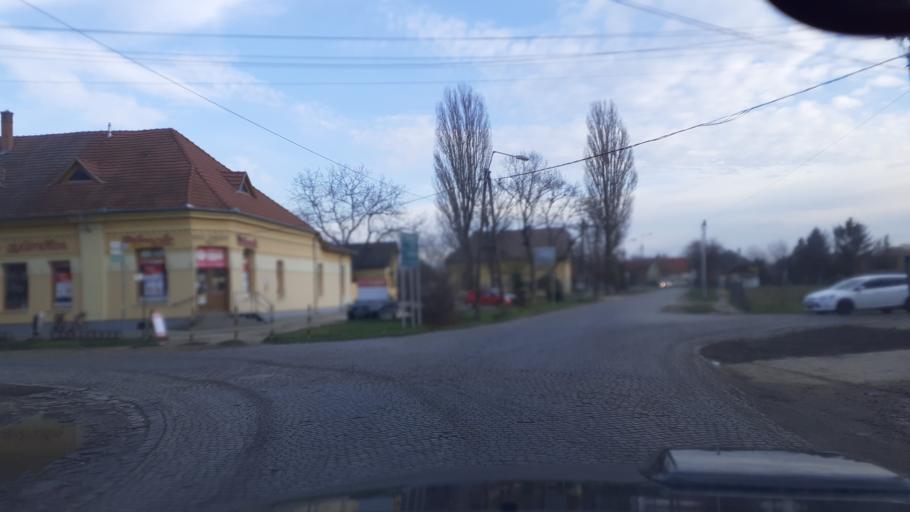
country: HU
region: Bacs-Kiskun
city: Kunszentmiklos
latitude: 47.0256
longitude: 19.1257
